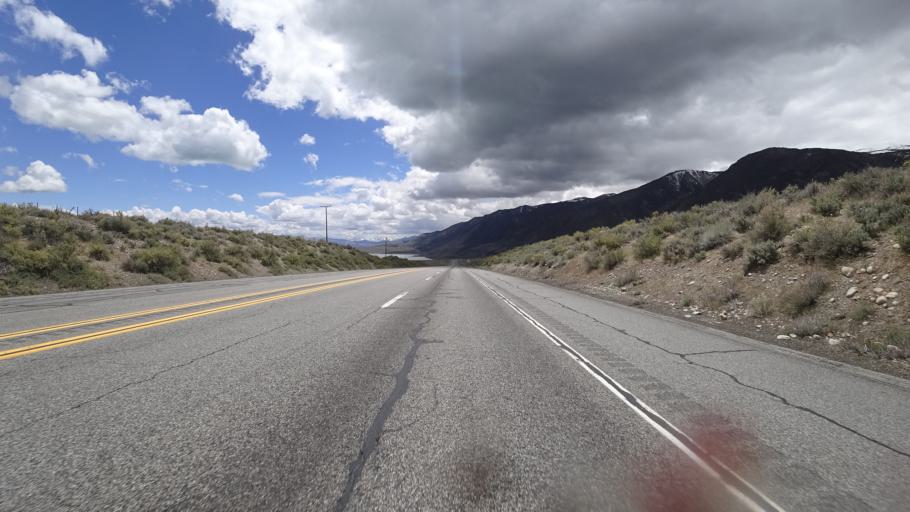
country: US
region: California
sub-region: Mono County
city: Bridgeport
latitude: 38.0374
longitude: -119.1582
